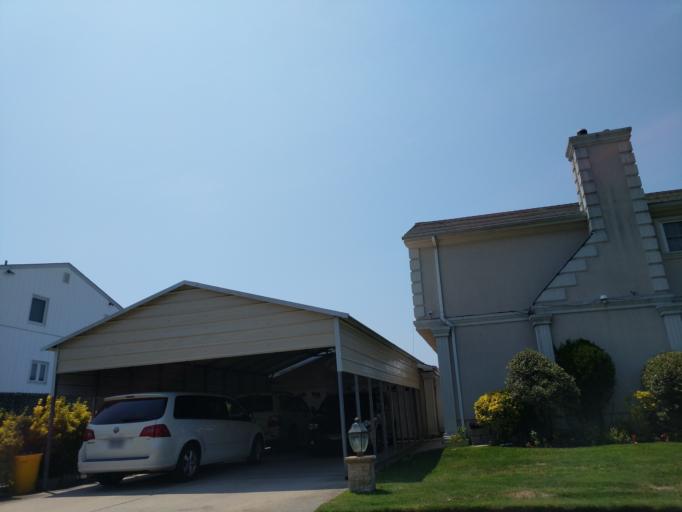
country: US
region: New York
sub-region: Nassau County
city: Cedarhurst
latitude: 40.6366
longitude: -73.7319
